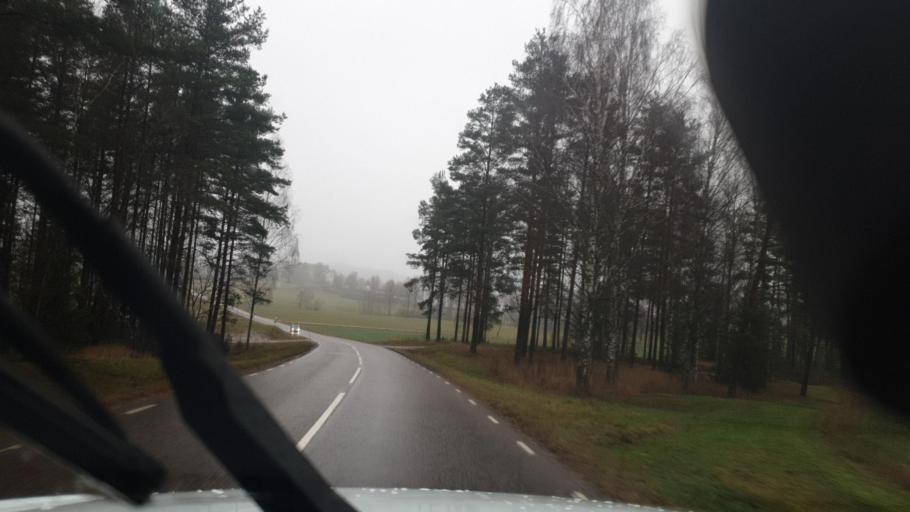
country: SE
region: Vaermland
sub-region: Arvika Kommun
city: Arvika
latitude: 59.6466
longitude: 12.8931
